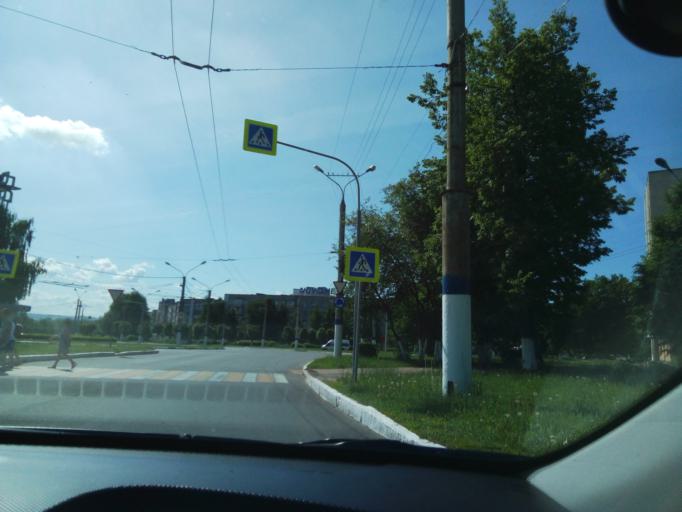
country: RU
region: Chuvashia
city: Novocheboksarsk
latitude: 56.1145
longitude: 47.4859
